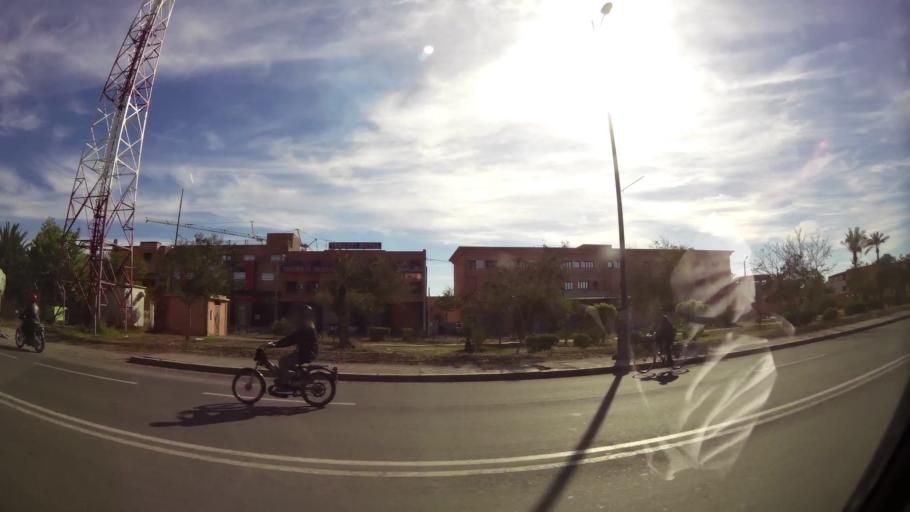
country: MA
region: Marrakech-Tensift-Al Haouz
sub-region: Marrakech
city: Marrakesh
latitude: 31.6743
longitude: -8.0436
